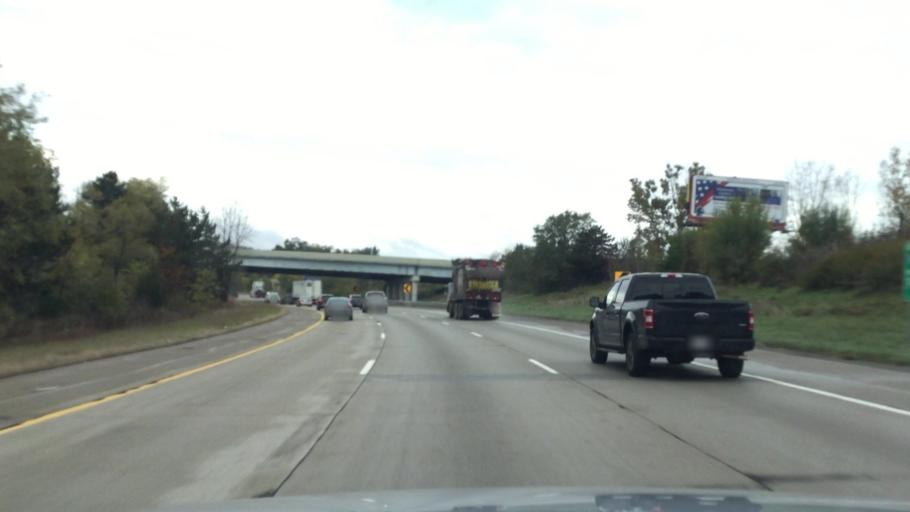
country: US
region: Michigan
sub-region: Washtenaw County
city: Ypsilanti
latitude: 42.2309
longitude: -83.5771
